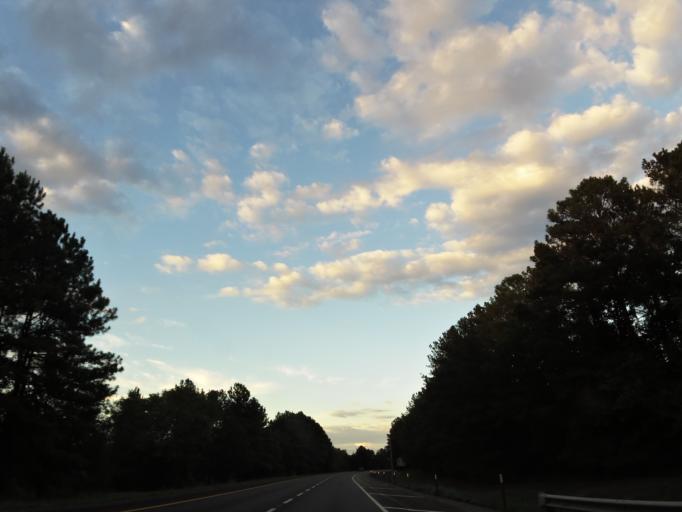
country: US
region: Tennessee
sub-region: Bradley County
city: Hopewell
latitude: 35.3211
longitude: -84.7909
